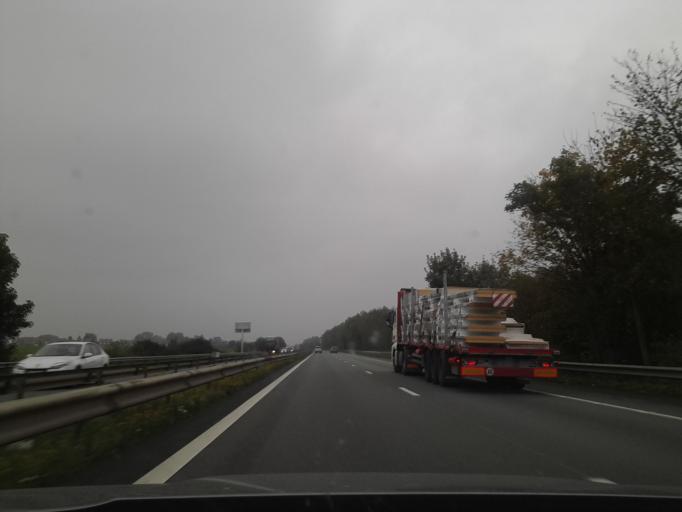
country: FR
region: Nord-Pas-de-Calais
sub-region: Departement du Nord
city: Lieu-Saint-Amand
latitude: 50.2825
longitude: 3.3471
